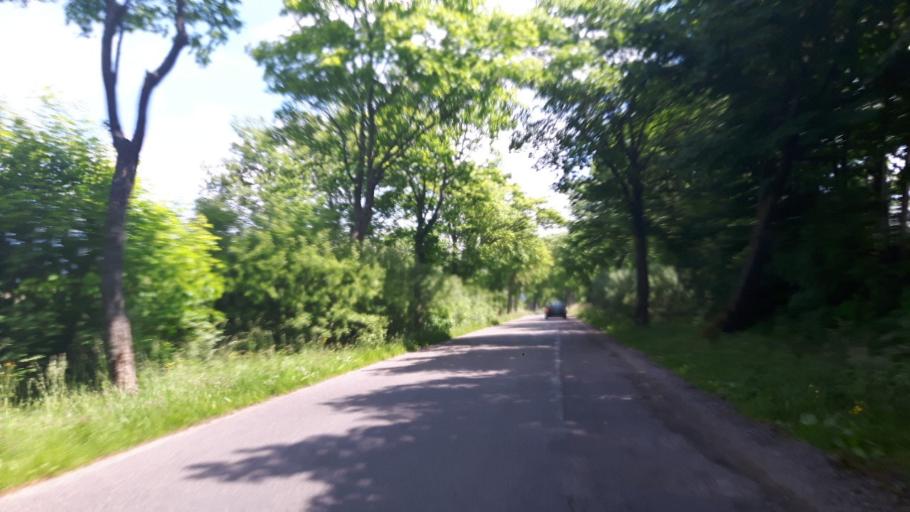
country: PL
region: West Pomeranian Voivodeship
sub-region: Powiat slawienski
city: Slawno
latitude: 54.5062
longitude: 16.6254
